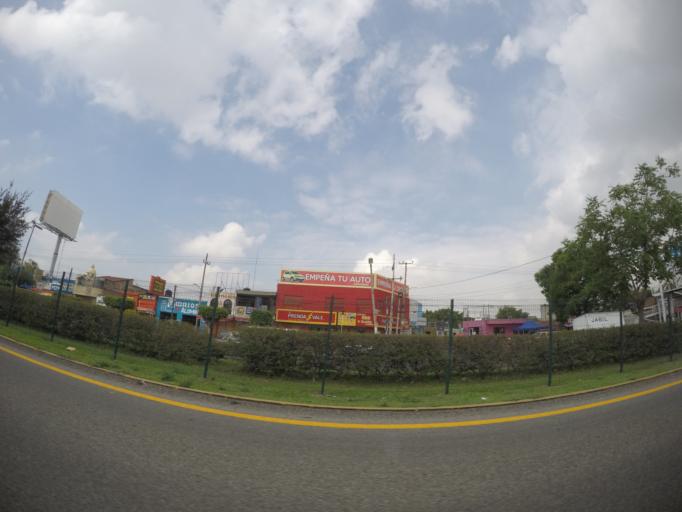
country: MX
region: Jalisco
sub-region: El Salto
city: Las Pintitas
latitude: 20.5587
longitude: -103.3064
